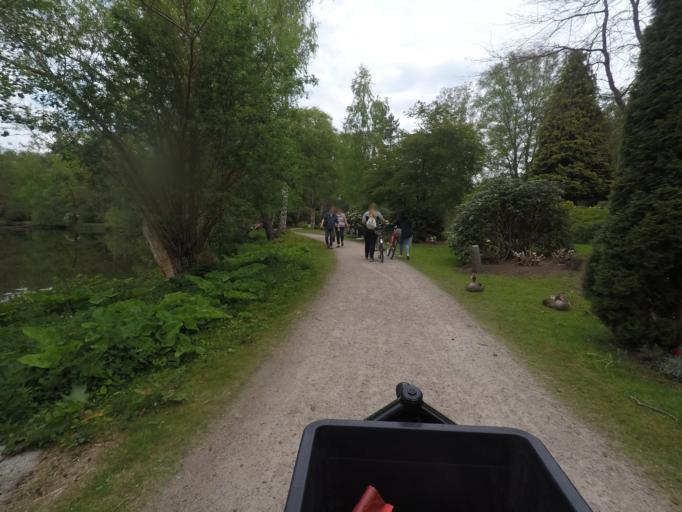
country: DE
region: Hamburg
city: Wellingsbuettel
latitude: 53.6280
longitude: 10.0679
